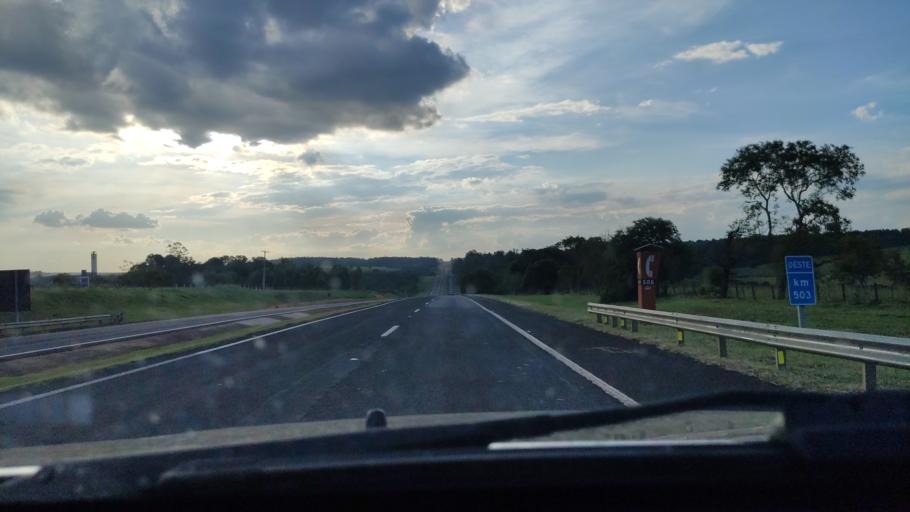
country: BR
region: Sao Paulo
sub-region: Rancharia
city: Rancharia
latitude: -22.4793
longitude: -50.9326
